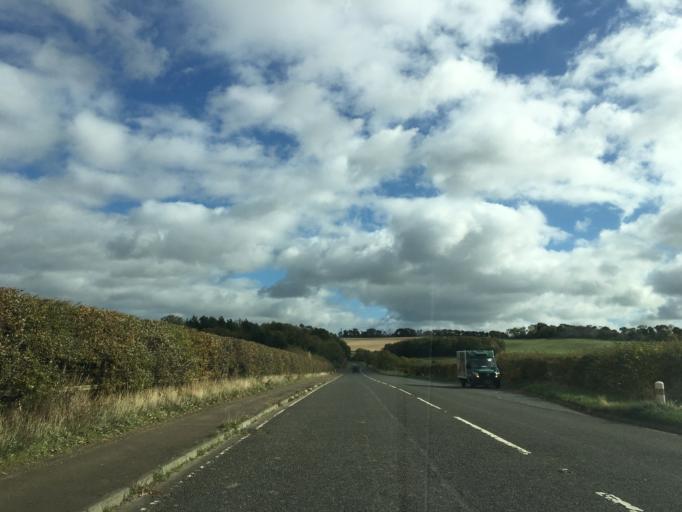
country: GB
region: Scotland
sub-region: Midlothian
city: Dalkeith
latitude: 55.8909
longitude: -3.0309
